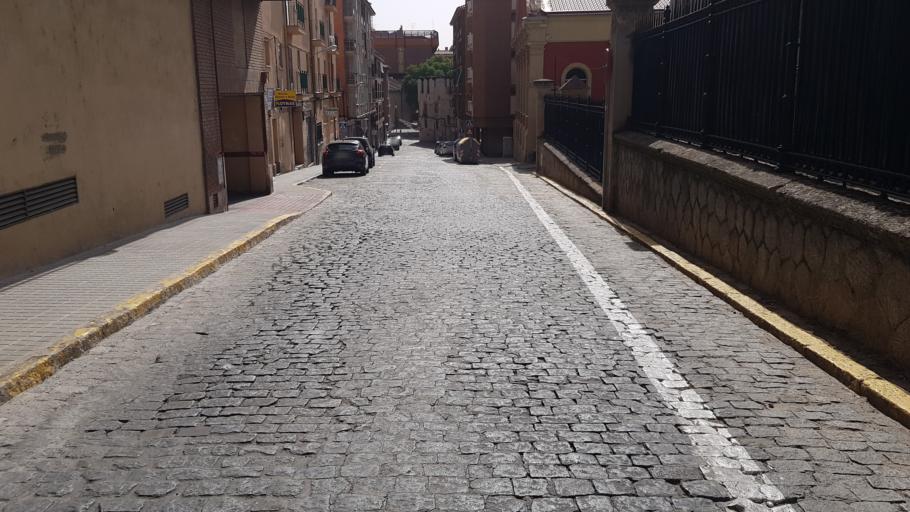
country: ES
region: Castille and Leon
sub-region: Provincia de Segovia
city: Segovia
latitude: 40.9455
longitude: -4.1142
